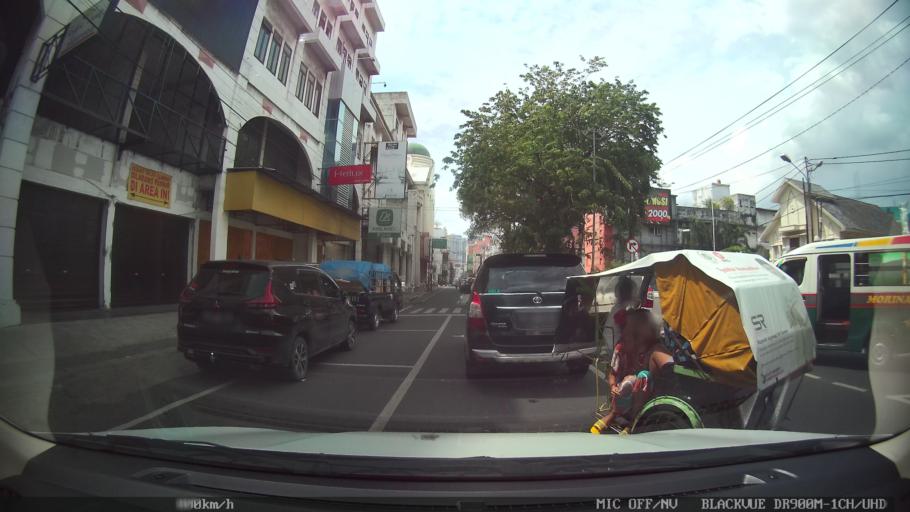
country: ID
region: North Sumatra
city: Medan
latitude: 3.5839
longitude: 98.6810
